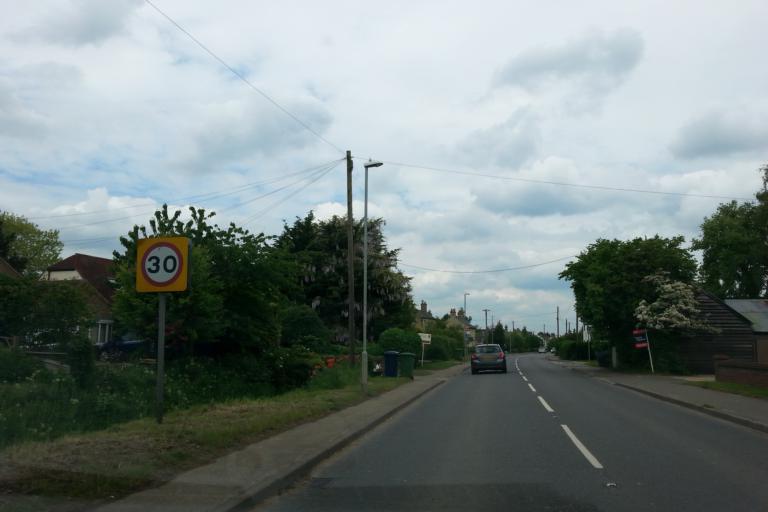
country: GB
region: England
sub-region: Cambridgeshire
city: Earith
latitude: 52.3069
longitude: 0.0530
